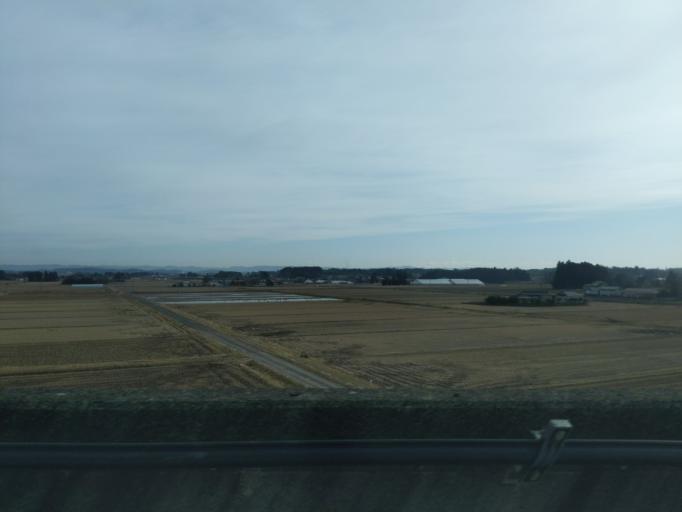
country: JP
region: Iwate
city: Ichinoseki
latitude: 38.7594
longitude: 141.0777
